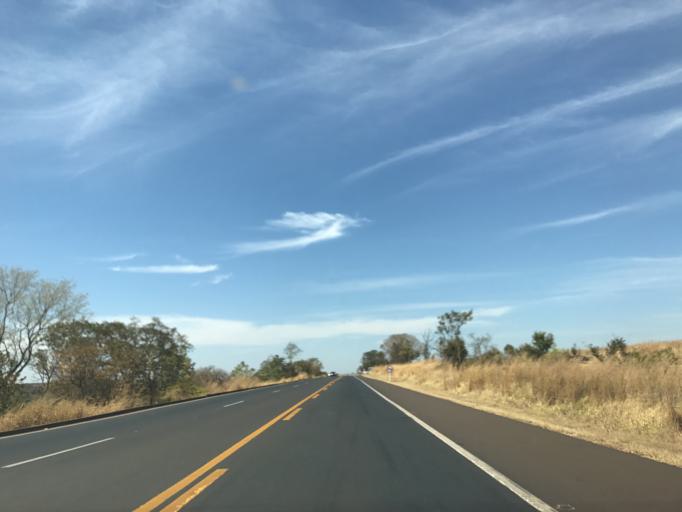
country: BR
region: Minas Gerais
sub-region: Monte Alegre De Minas
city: Monte Alegre de Minas
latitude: -18.9216
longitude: -49.0338
